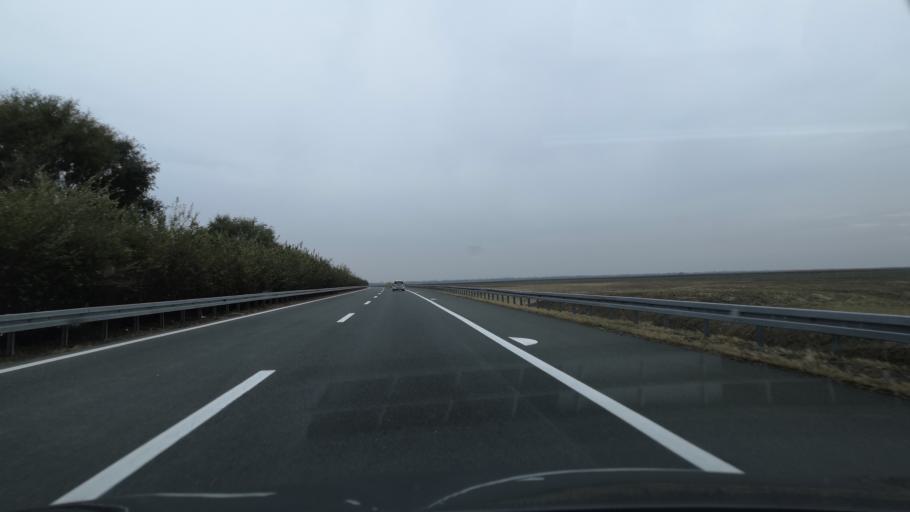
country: RS
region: Autonomna Pokrajina Vojvodina
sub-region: Severnobacki Okrug
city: Mali Igos
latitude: 45.6751
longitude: 19.7289
